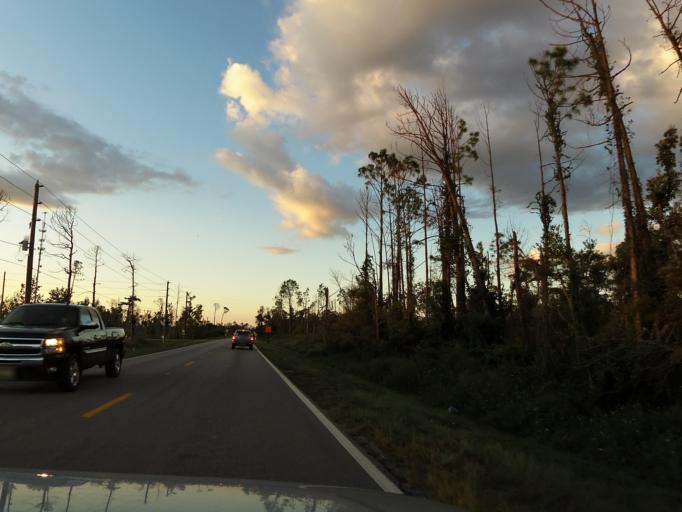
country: US
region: Florida
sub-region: Bay County
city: Mexico Beach
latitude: 29.9397
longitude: -85.3887
